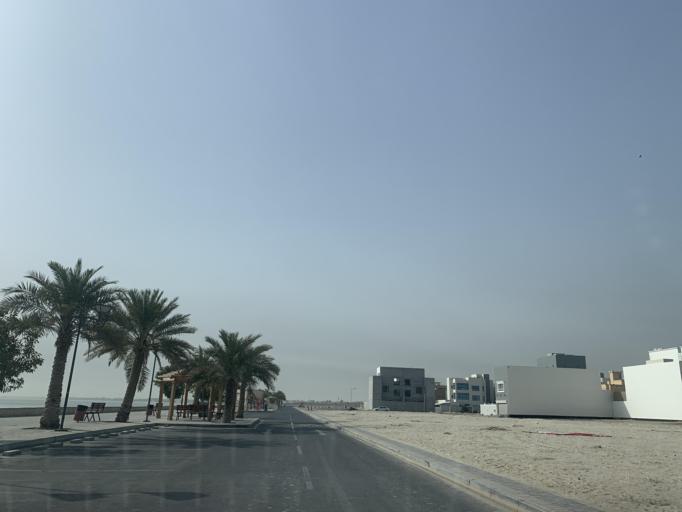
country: BH
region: Northern
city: Madinat `Isa
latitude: 26.1897
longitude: 50.5666
